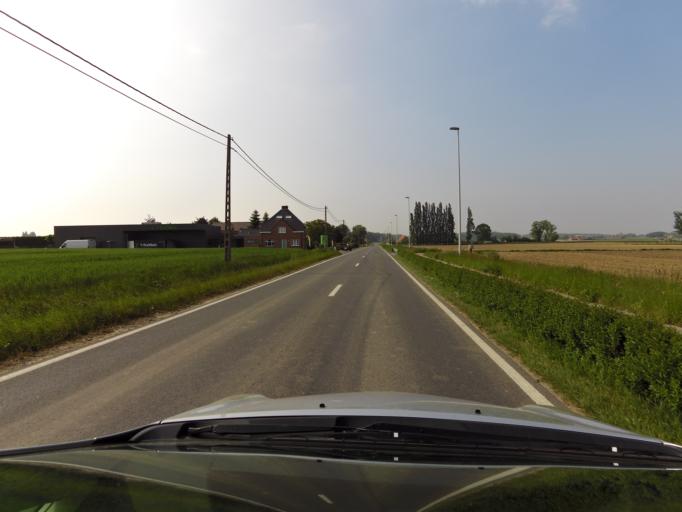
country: BE
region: Flanders
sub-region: Provincie West-Vlaanderen
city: Poperinge
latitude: 50.8738
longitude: 2.7076
